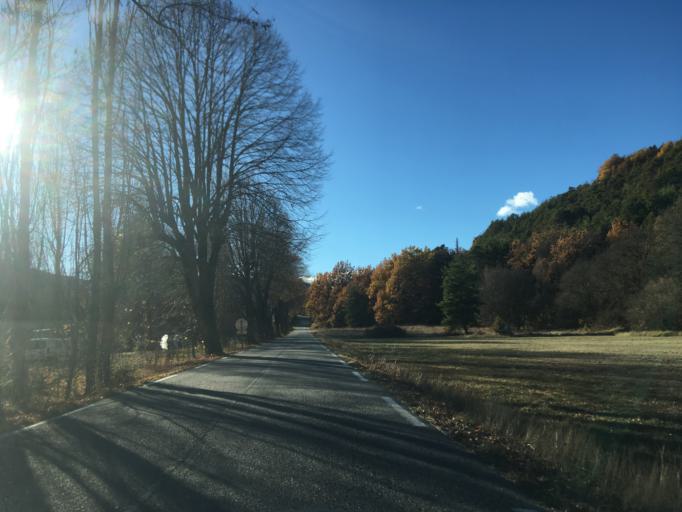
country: FR
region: Provence-Alpes-Cote d'Azur
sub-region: Departement des Alpes-de-Haute-Provence
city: Castellane
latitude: 43.7423
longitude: 6.4973
